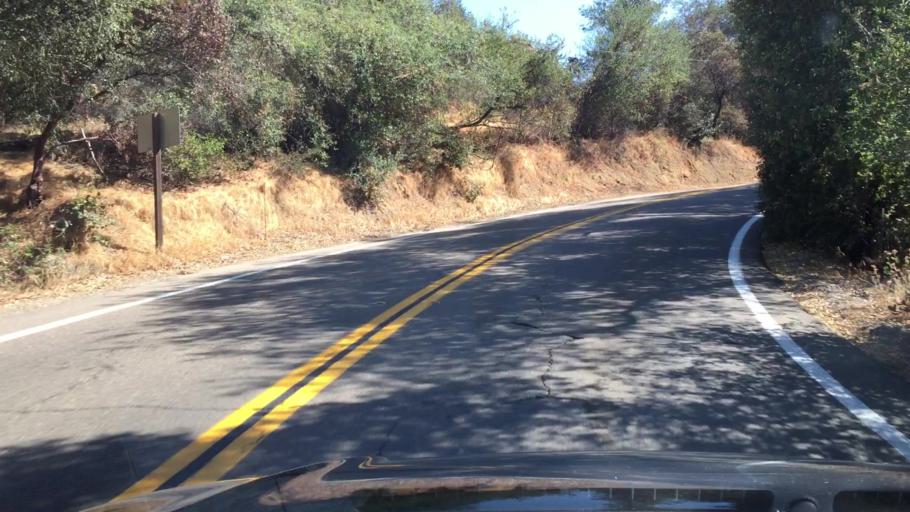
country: US
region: California
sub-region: San Diego County
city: Harbison Canyon
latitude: 32.7493
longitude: -116.7884
